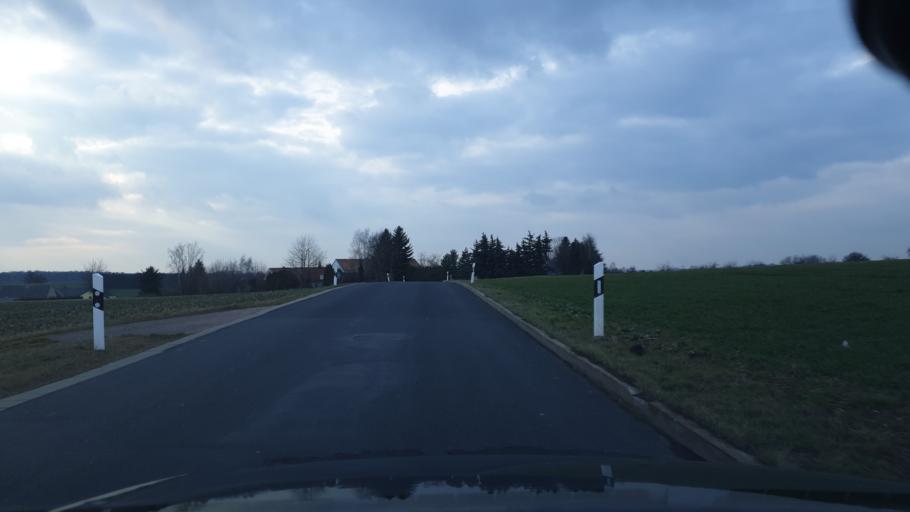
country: DE
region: Saxony
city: Erlau
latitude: 50.9901
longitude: 12.9196
